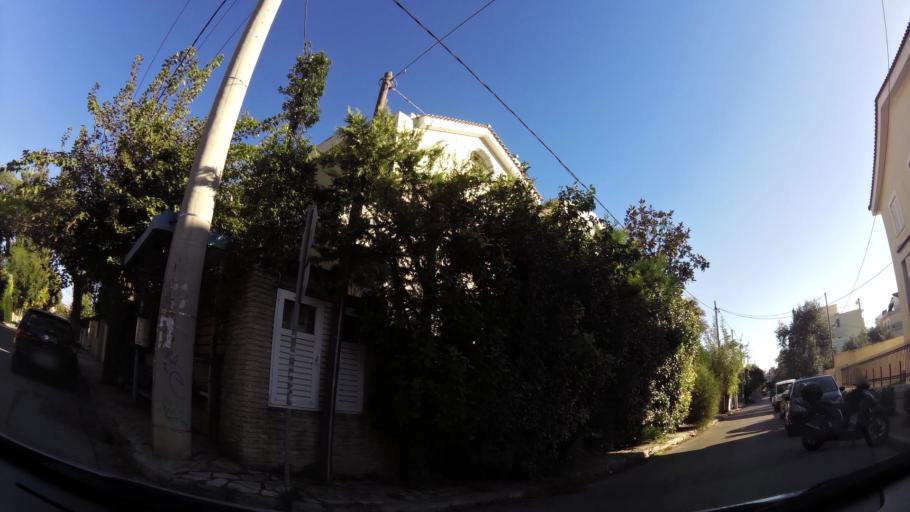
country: GR
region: Attica
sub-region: Nomarchia Athinas
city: Kifisia
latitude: 38.0783
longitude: 23.7974
